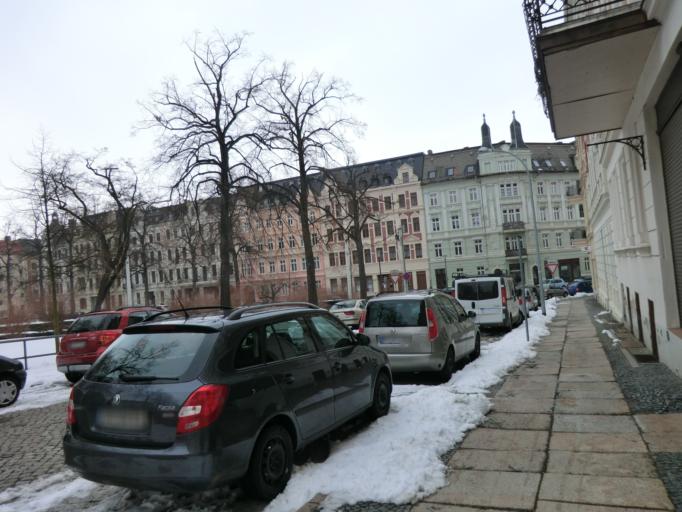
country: DE
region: Saxony
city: Goerlitz
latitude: 51.1438
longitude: 14.9760
